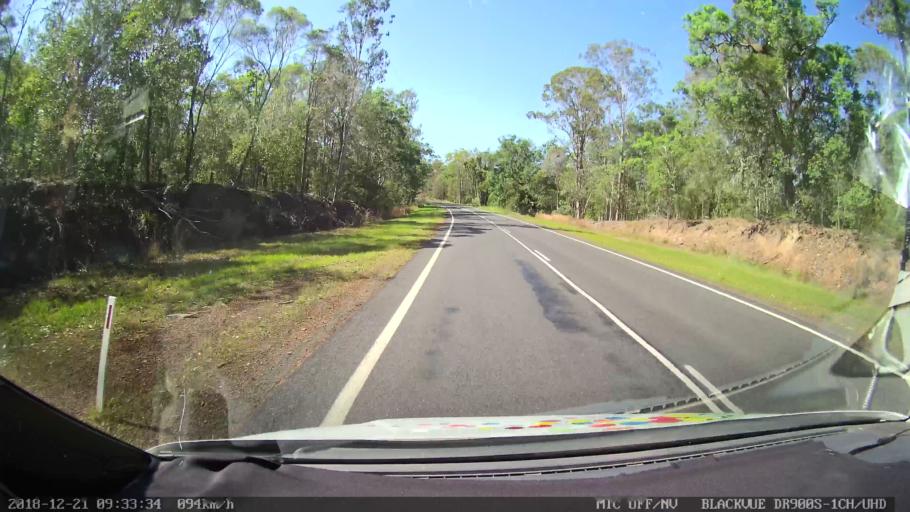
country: AU
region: New South Wales
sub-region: Clarence Valley
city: Grafton
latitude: -29.4864
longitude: 152.9766
